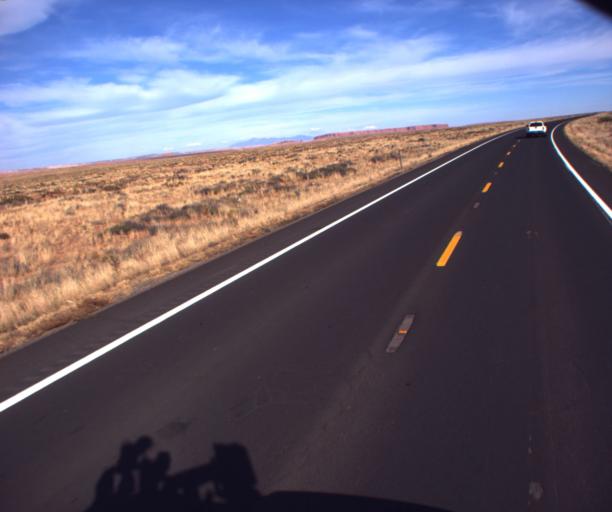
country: US
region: Arizona
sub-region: Apache County
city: Lukachukai
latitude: 36.9638
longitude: -109.4782
